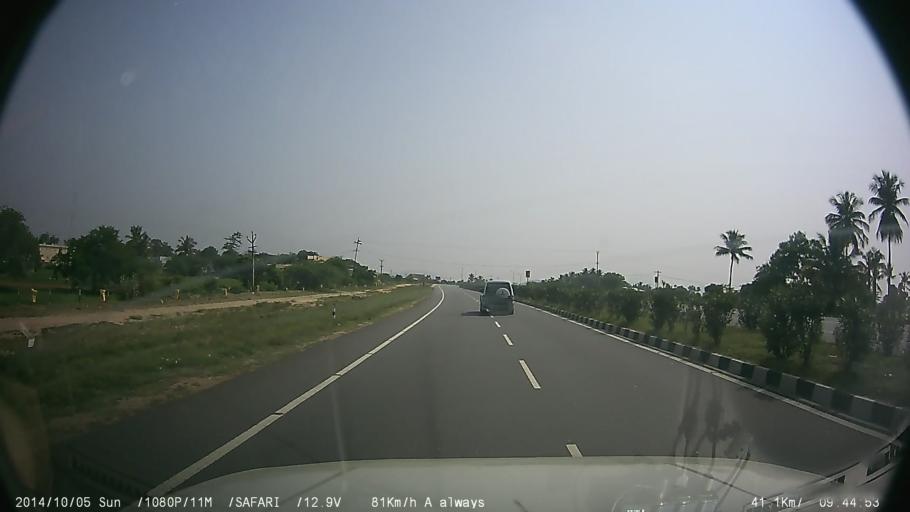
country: IN
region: Tamil Nadu
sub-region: Erode
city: Bhavani
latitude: 11.4508
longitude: 77.7776
